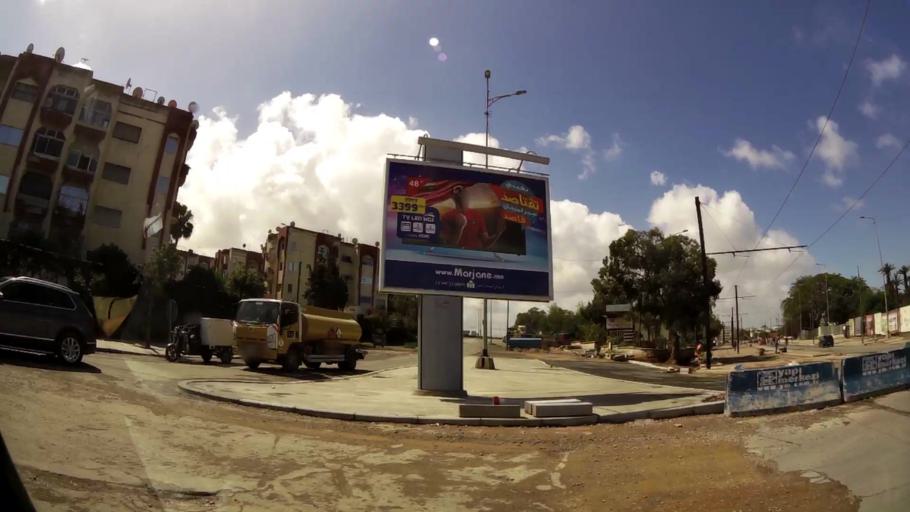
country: MA
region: Grand Casablanca
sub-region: Mediouna
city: Tit Mellil
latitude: 33.6052
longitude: -7.5277
